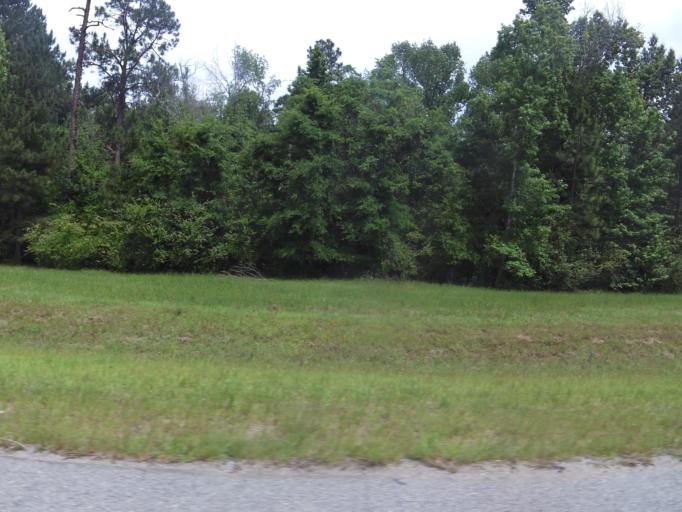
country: US
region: Georgia
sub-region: Emanuel County
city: Swainsboro
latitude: 32.5982
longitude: -82.3758
